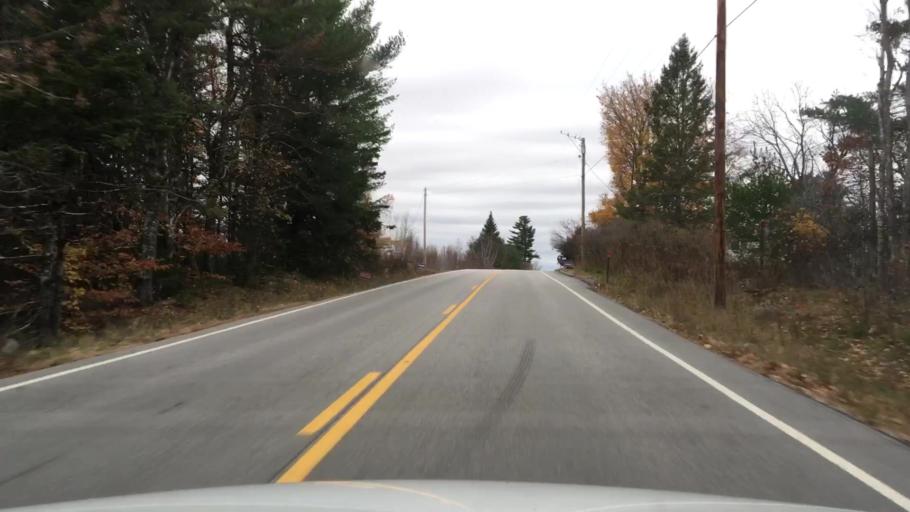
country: US
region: Maine
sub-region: Hancock County
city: Orland
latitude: 44.5455
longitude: -68.6878
